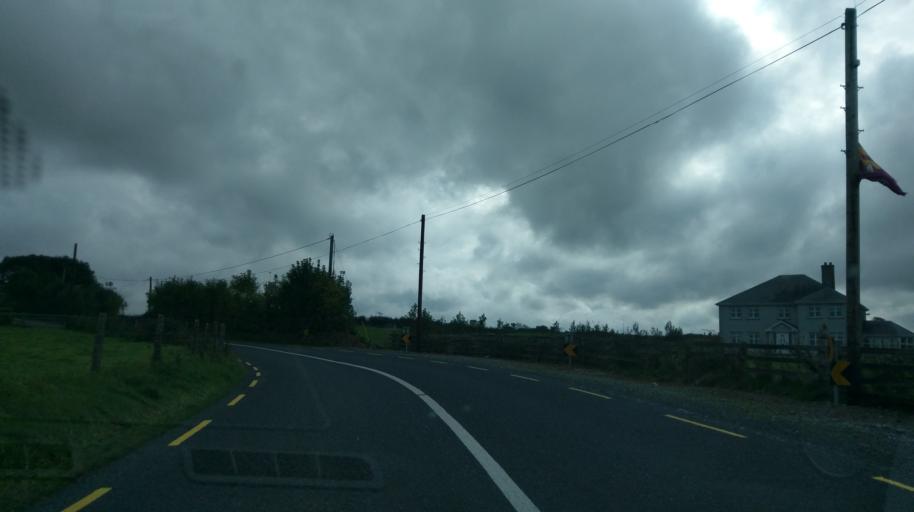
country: IE
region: Connaught
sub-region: County Galway
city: Loughrea
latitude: 53.4443
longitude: -8.4663
